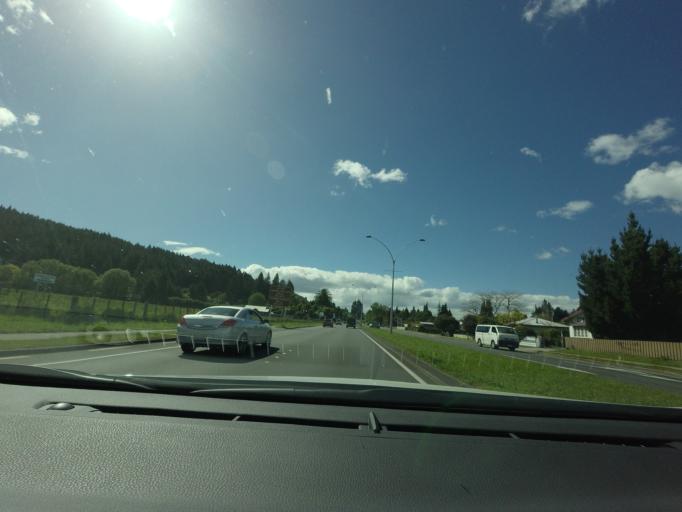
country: NZ
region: Bay of Plenty
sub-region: Rotorua District
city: Rotorua
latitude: -38.1122
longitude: 176.2243
